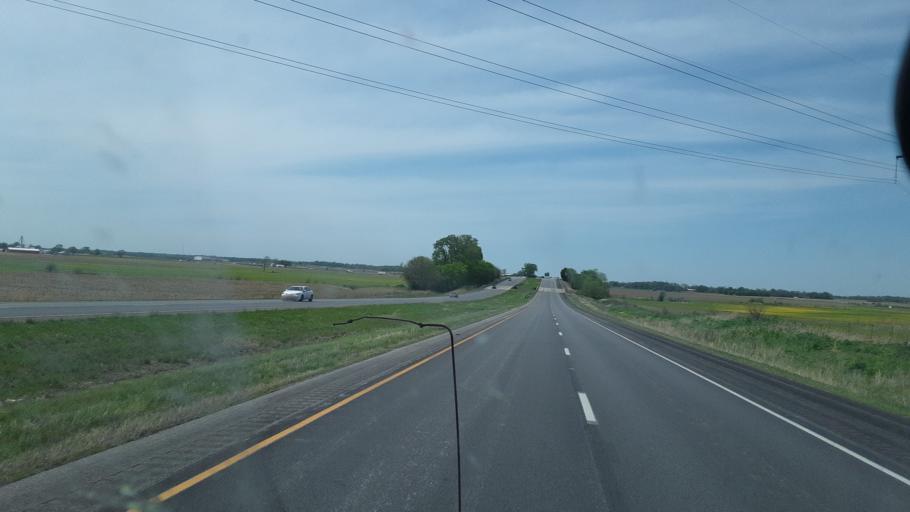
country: US
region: Indiana
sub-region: Posey County
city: Poseyville
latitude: 38.1771
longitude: -87.7593
